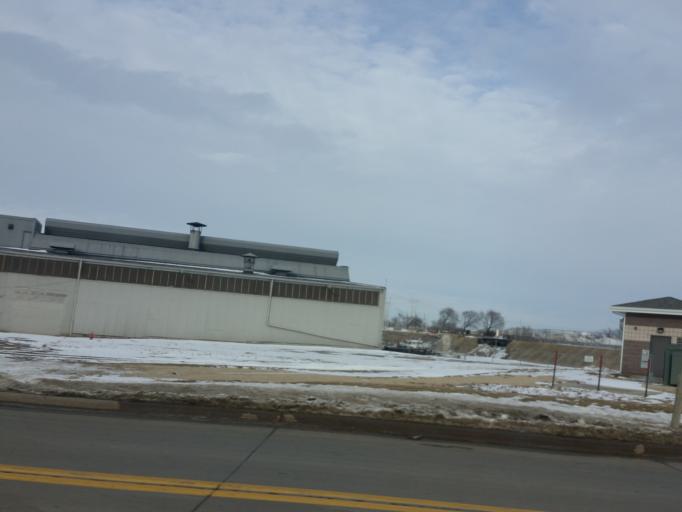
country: US
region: Iowa
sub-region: Black Hawk County
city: Waterloo
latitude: 42.5004
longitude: -92.3480
